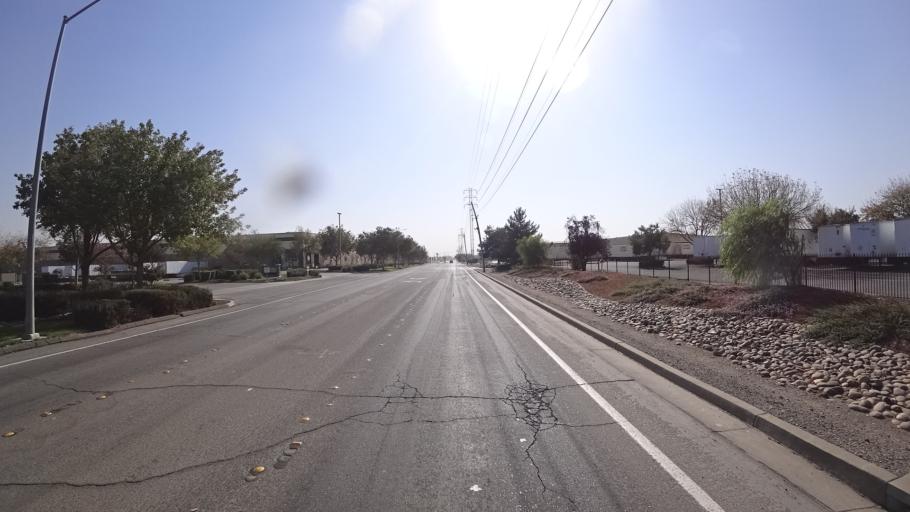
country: US
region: California
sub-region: Yolo County
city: Woodland
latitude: 38.6887
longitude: -121.7469
